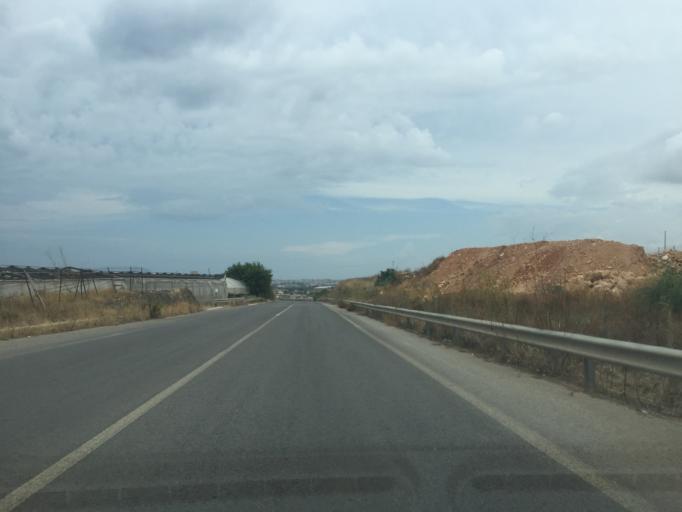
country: IT
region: Sicily
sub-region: Ragusa
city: Donnalucata
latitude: 36.7728
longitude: 14.6224
